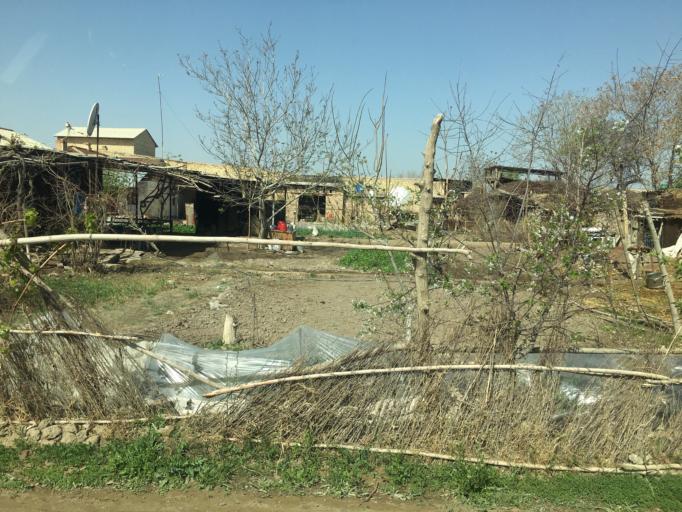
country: TM
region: Lebap
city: Turkmenabat
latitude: 38.9611
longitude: 63.6497
